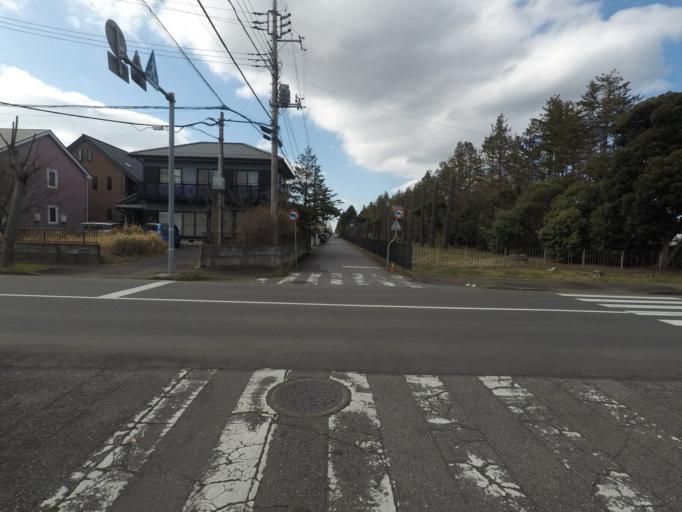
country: JP
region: Ibaraki
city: Ushiku
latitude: 36.0262
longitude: 140.0985
